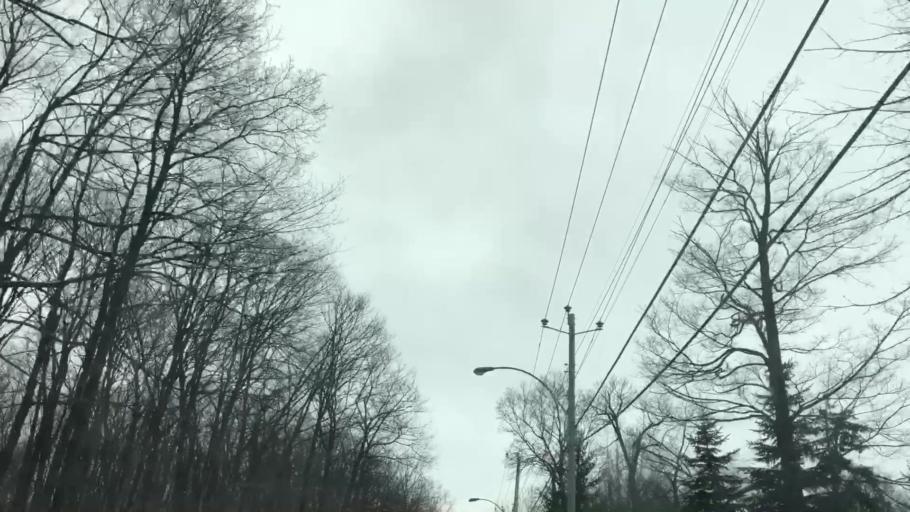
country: CA
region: Quebec
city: Dorval
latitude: 45.5164
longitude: -73.7455
